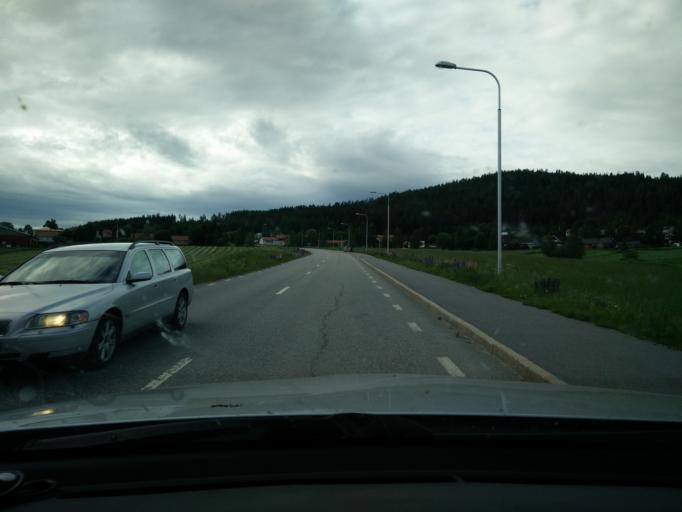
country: SE
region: Gaevleborg
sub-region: Hudiksvalls Kommun
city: Delsbo
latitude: 62.1058
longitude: 16.7185
